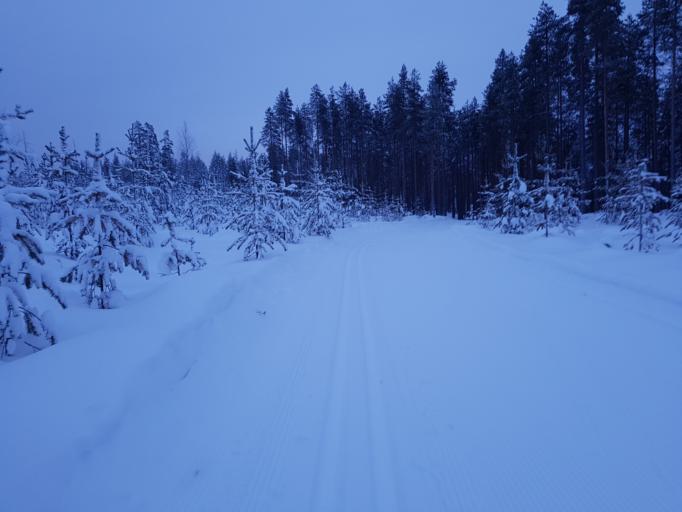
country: FI
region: Kainuu
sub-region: Kehys-Kainuu
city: Kuhmo
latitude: 64.0859
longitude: 29.5176
